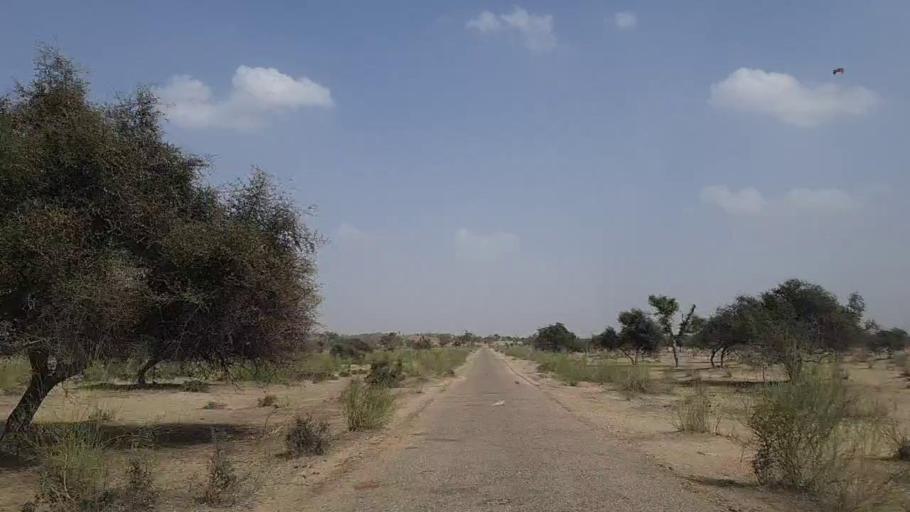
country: PK
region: Sindh
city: Islamkot
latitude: 24.7996
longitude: 70.1223
